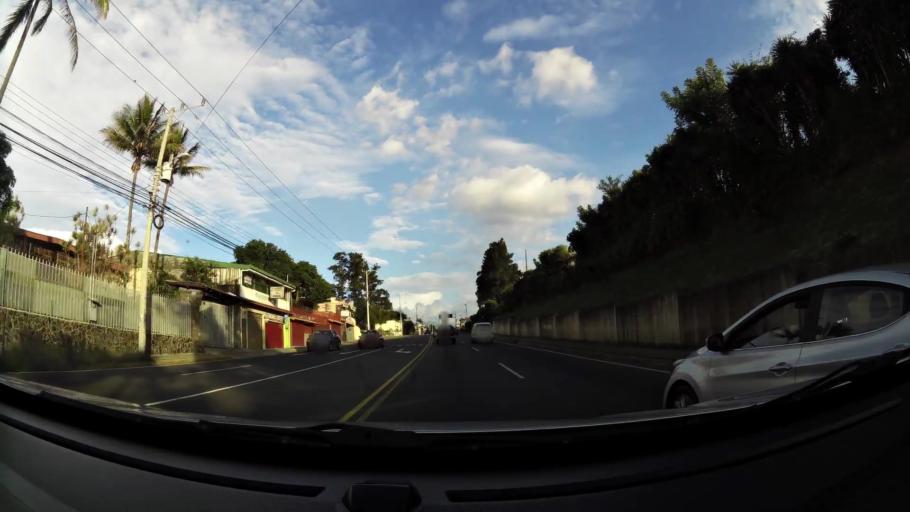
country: CR
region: Heredia
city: San Francisco
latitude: 9.9968
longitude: -84.1365
